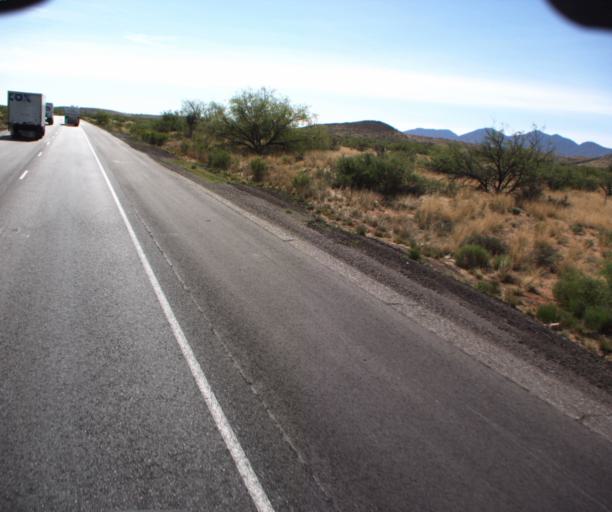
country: US
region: Arizona
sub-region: Cochise County
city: Mescal
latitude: 31.9746
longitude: -110.5056
